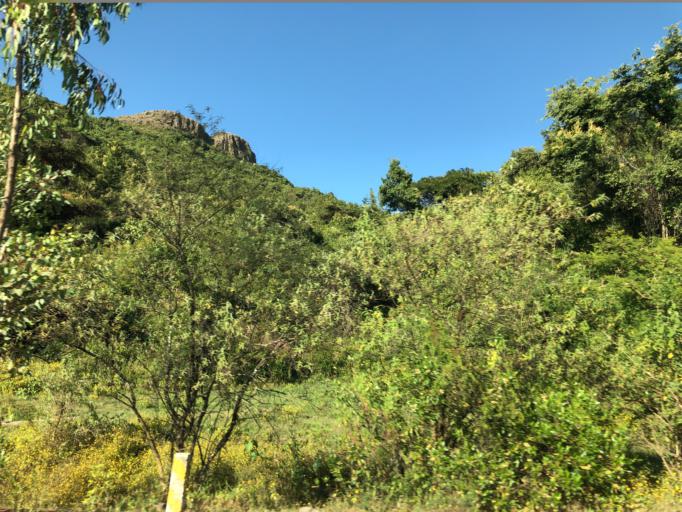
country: ET
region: Amhara
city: Debre Tabor
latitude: 11.9260
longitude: 37.9465
